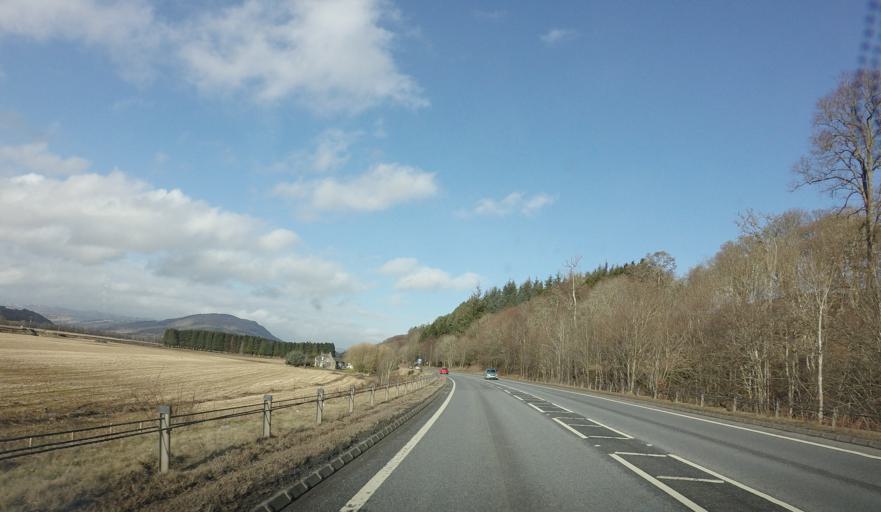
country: GB
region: Scotland
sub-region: Perth and Kinross
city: Pitlochry
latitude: 56.6350
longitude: -3.6447
